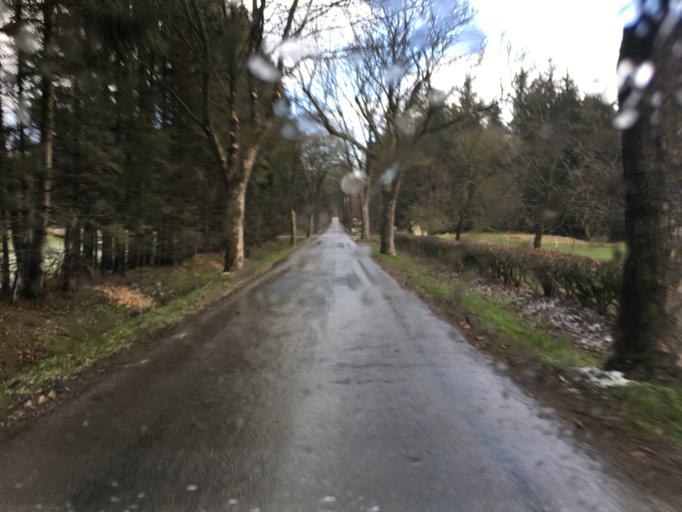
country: DE
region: North Rhine-Westphalia
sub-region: Regierungsbezirk Koln
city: Hurtgenwald
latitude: 50.6741
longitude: 6.3166
